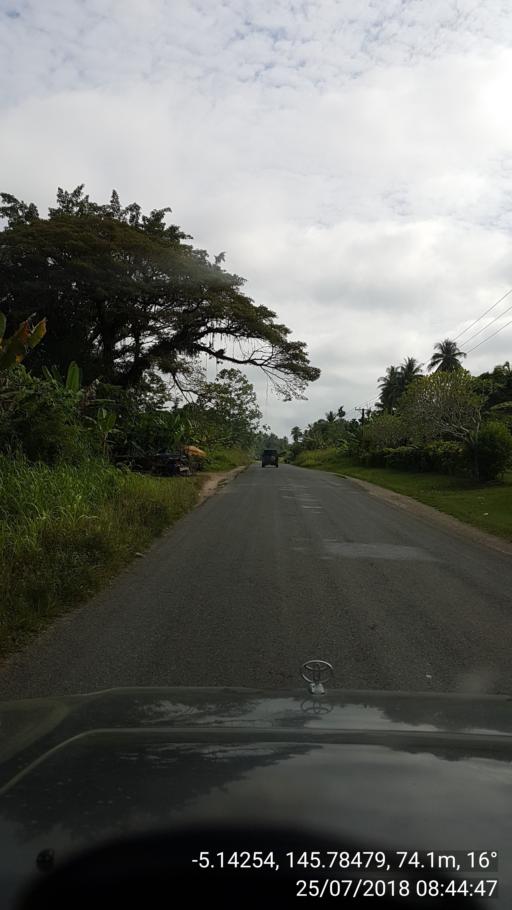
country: PG
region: Madang
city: Madang
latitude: -5.1428
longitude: 145.7847
